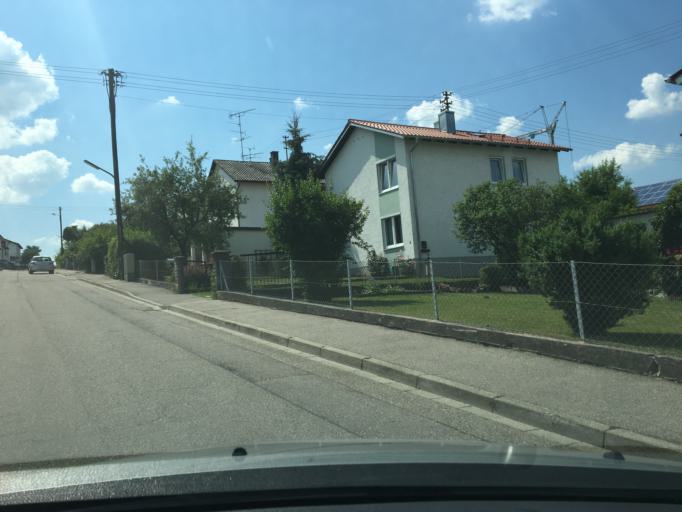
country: DE
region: Bavaria
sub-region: Upper Bavaria
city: Neumarkt-Sankt Veit
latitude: 48.3571
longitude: 12.5108
